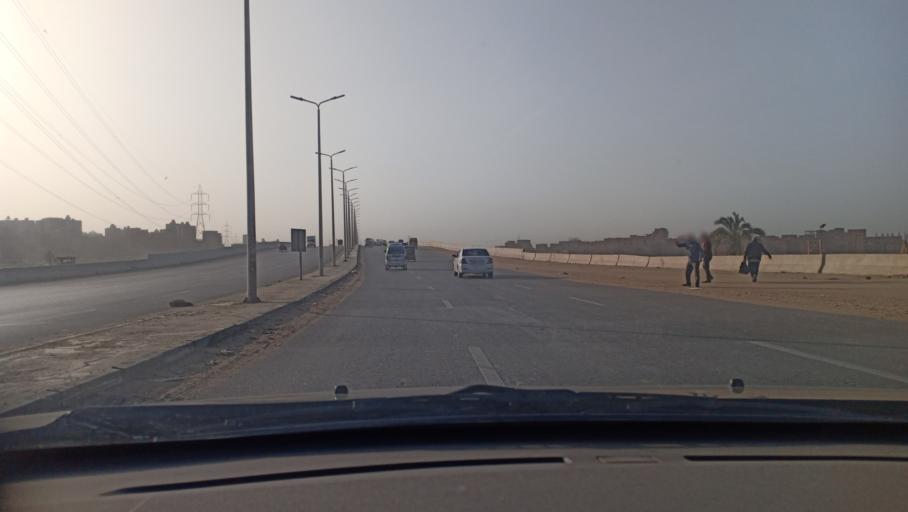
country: EG
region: Muhafazat al Qalyubiyah
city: Qalyub
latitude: 30.1417
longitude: 31.2636
